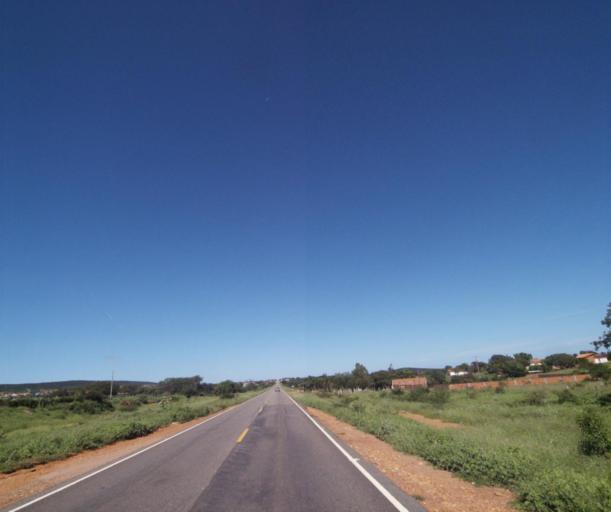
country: BR
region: Bahia
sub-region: Palmas De Monte Alto
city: Palmas de Monte Alto
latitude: -14.2484
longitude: -43.1493
